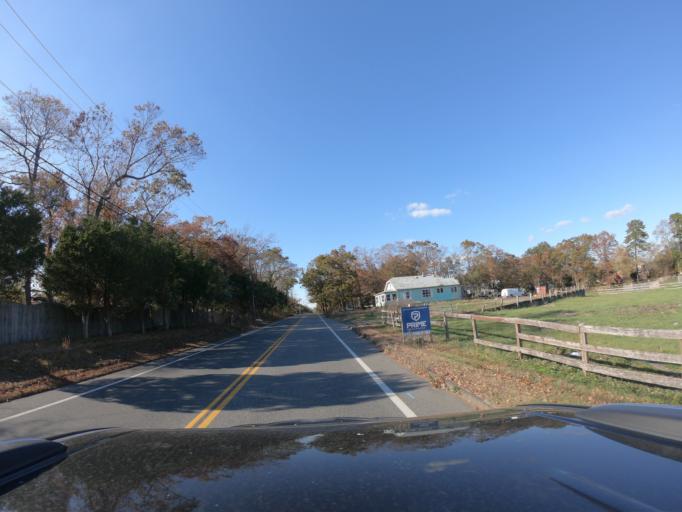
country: US
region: New Jersey
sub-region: Monmouth County
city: Ramtown
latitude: 40.0930
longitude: -74.1569
